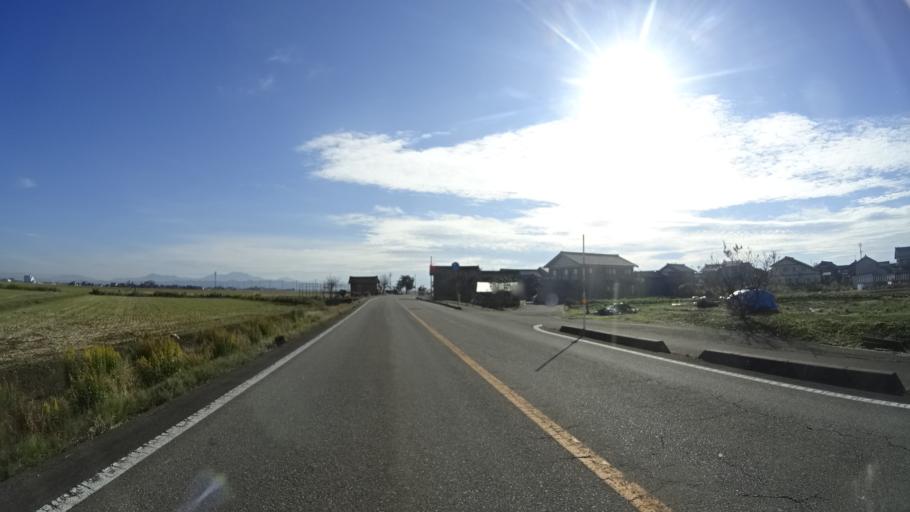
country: JP
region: Niigata
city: Mitsuke
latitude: 37.5750
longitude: 138.8393
